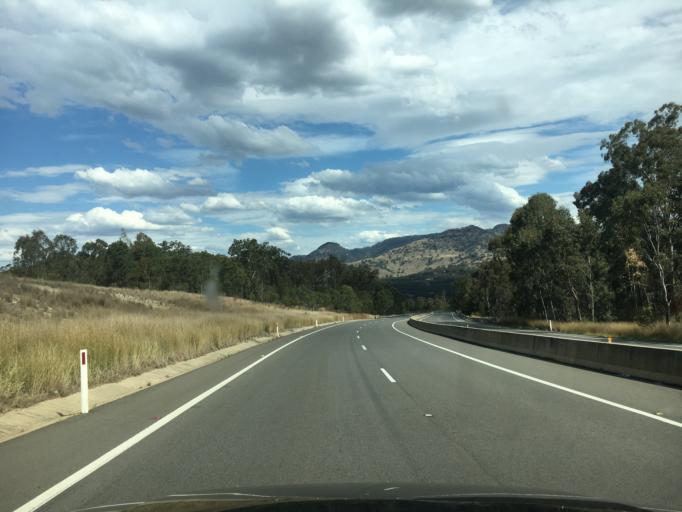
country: AU
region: New South Wales
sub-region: Liverpool Plains
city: Quirindi
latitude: -31.7434
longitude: 150.8052
